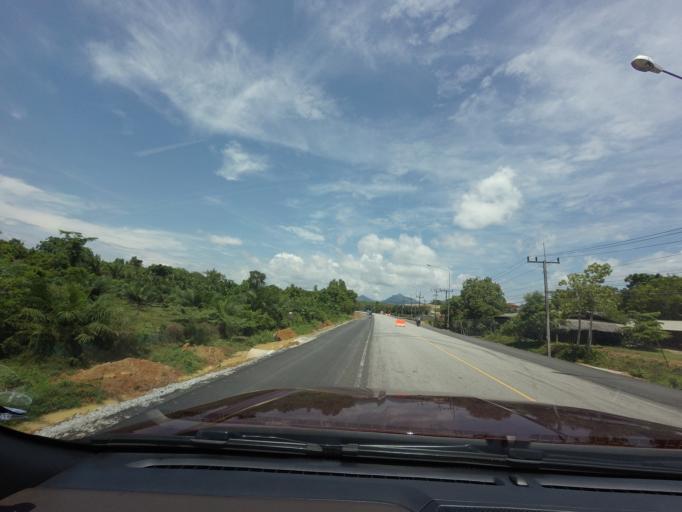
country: TH
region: Narathiwat
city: Ra-ngae
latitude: 6.2843
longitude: 101.7022
